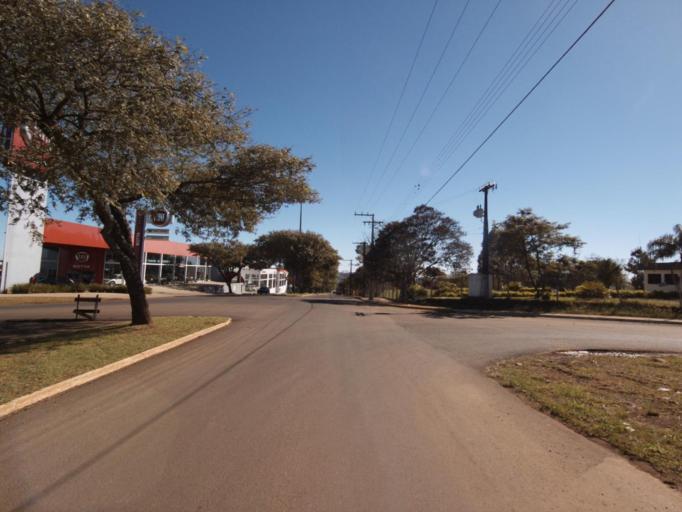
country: BR
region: Santa Catarina
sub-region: Xanxere
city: Xanxere
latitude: -26.8820
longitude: -52.3813
